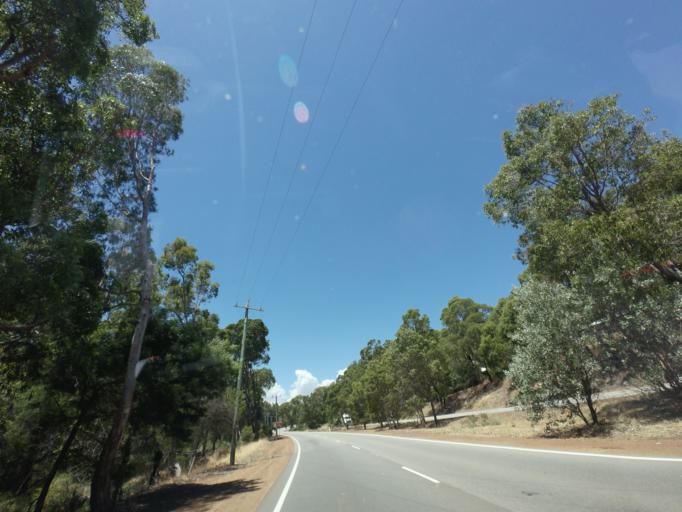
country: AU
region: Western Australia
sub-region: Mundaring
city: Parkerville
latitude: -31.8996
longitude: 116.1367
